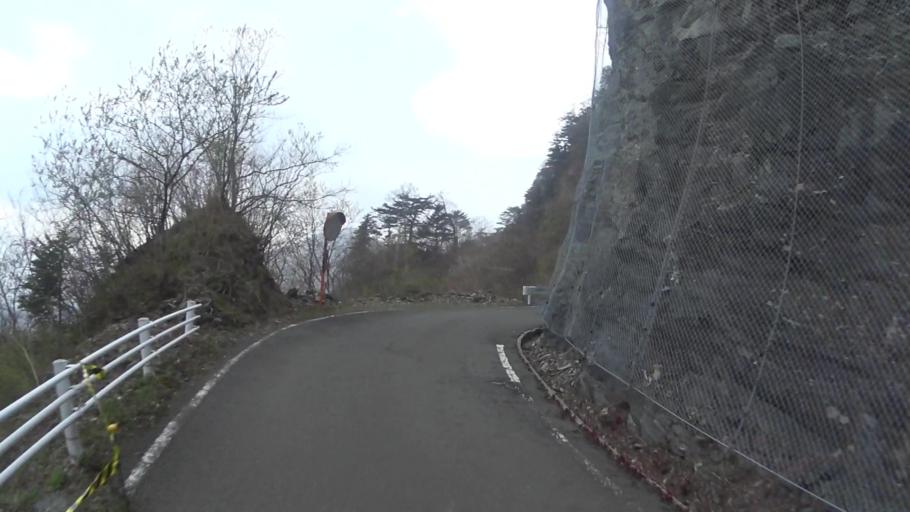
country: JP
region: Ehime
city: Saijo
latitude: 33.7804
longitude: 133.2378
